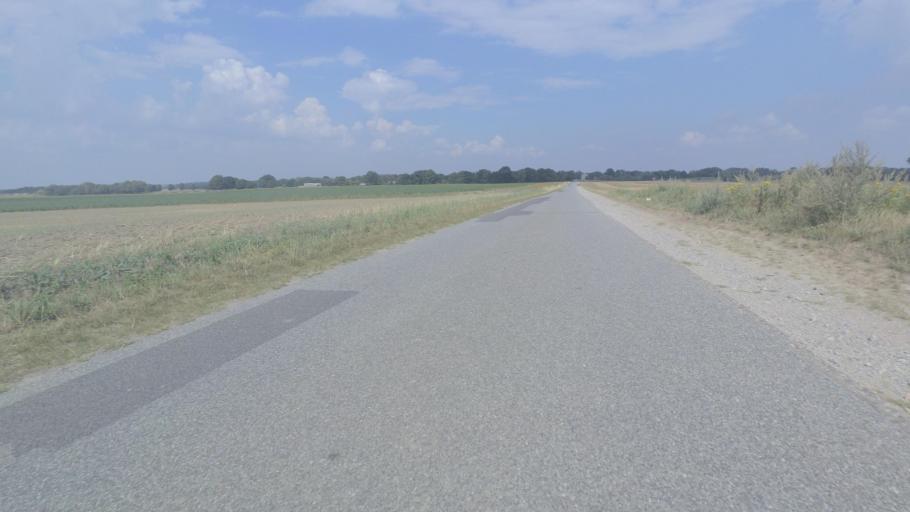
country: DE
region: Mecklenburg-Vorpommern
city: Borrentin
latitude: 53.8457
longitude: 12.9495
